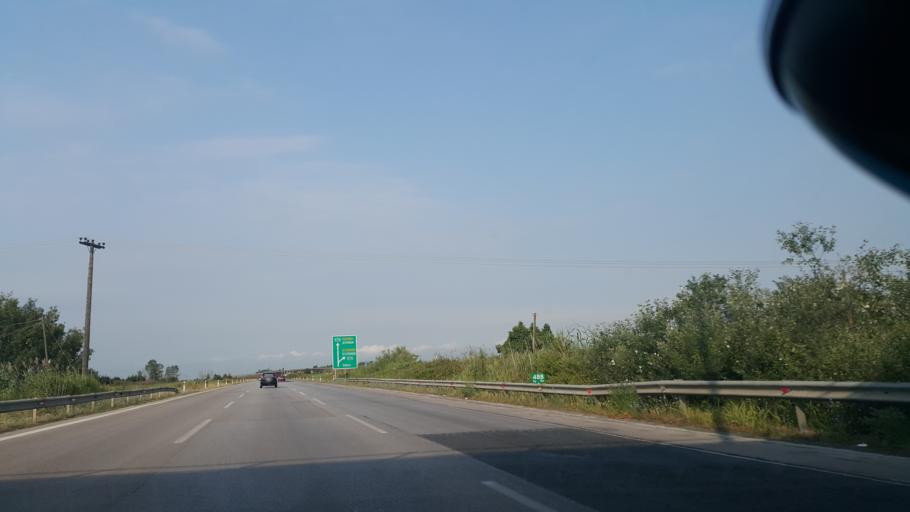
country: GR
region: Central Macedonia
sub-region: Nomos Thessalonikis
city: Chalastra
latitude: 40.6140
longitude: 22.7425
